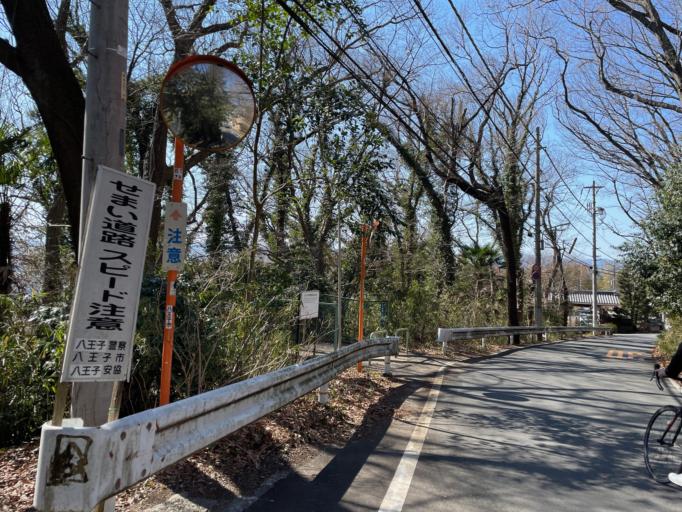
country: JP
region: Tokyo
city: Hachioji
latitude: 35.6735
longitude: 139.3358
